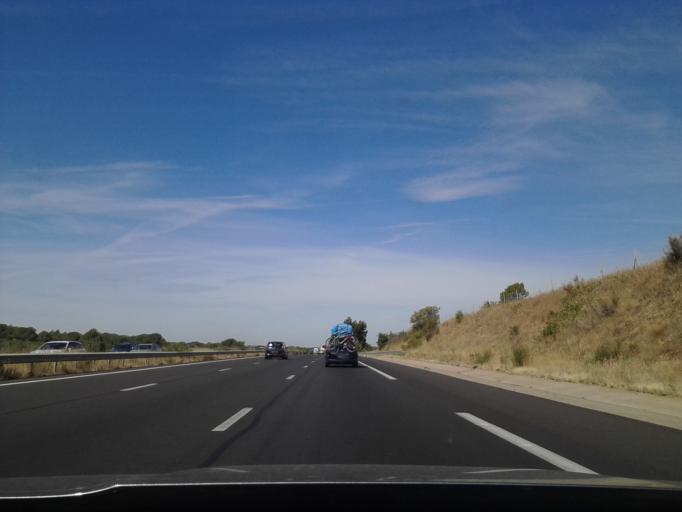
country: FR
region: Languedoc-Roussillon
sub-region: Departement de l'Aude
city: Fleury
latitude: 43.2303
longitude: 3.1160
